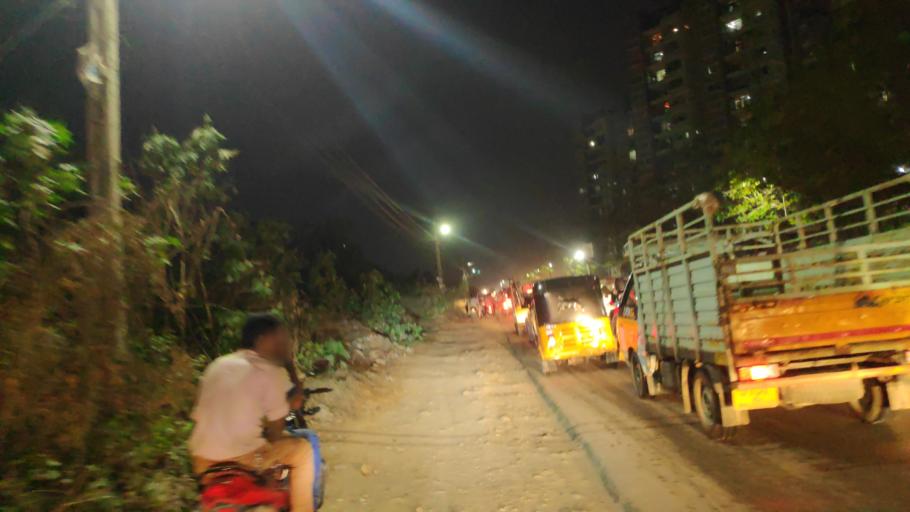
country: IN
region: Telangana
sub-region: Rangareddi
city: Kukatpalli
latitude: 17.4750
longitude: 78.3816
